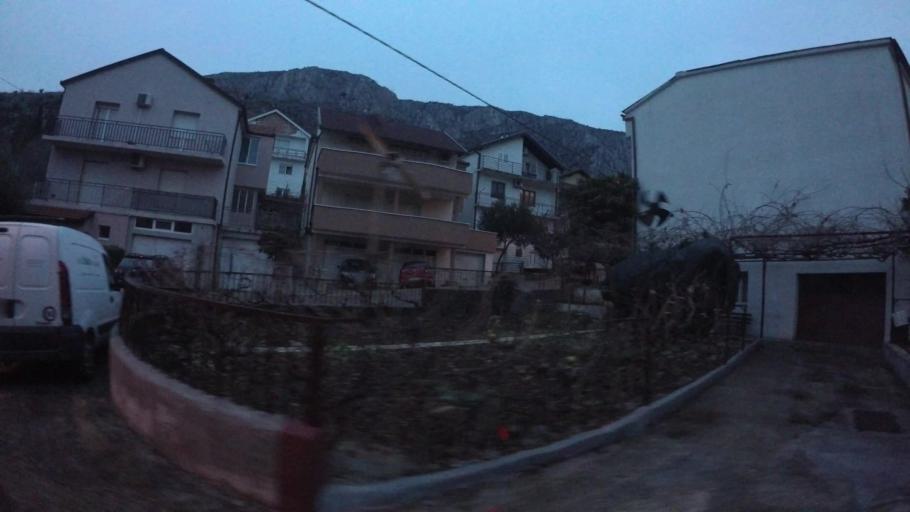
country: BA
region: Federation of Bosnia and Herzegovina
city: Rodoc
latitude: 43.3237
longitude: 17.8186
